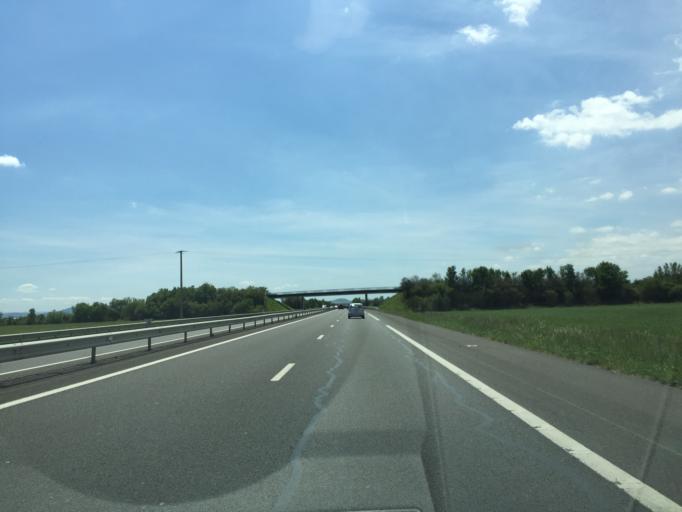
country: FR
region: Auvergne
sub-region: Departement du Puy-de-Dome
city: Menetrol
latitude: 45.8820
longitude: 3.1543
